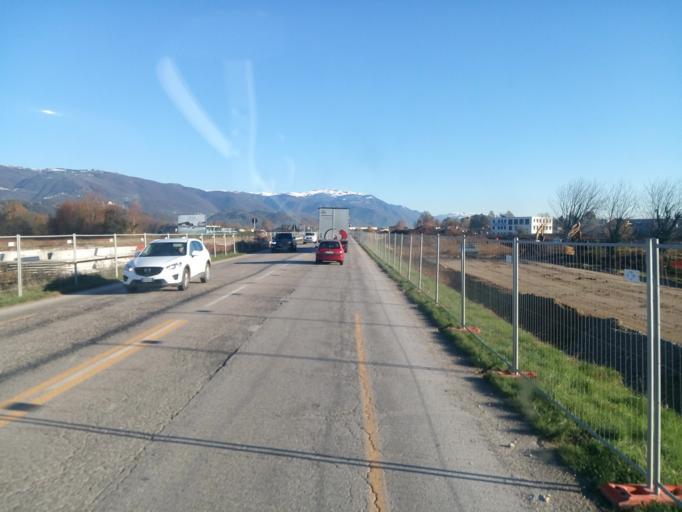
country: IT
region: Veneto
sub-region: Provincia di Vicenza
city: Schiavon
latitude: 45.7201
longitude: 11.6417
